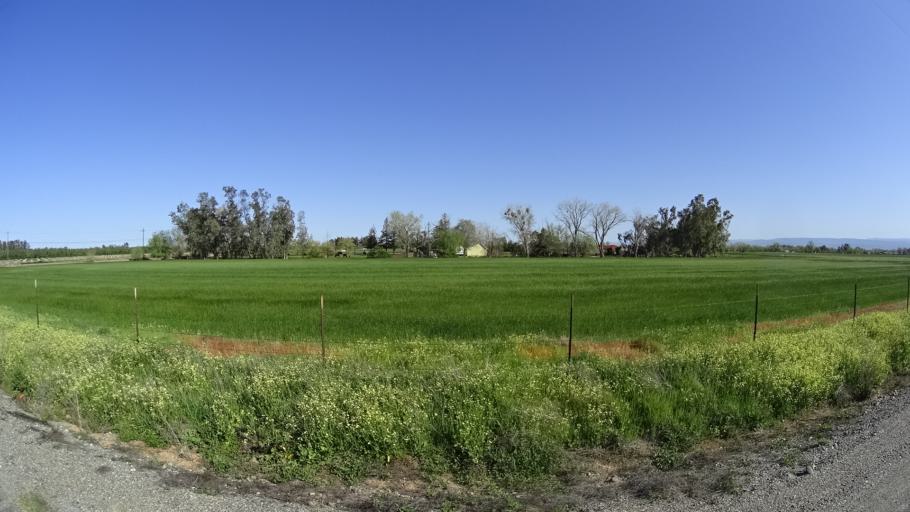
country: US
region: California
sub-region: Glenn County
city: Hamilton City
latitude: 39.7754
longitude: -122.0651
